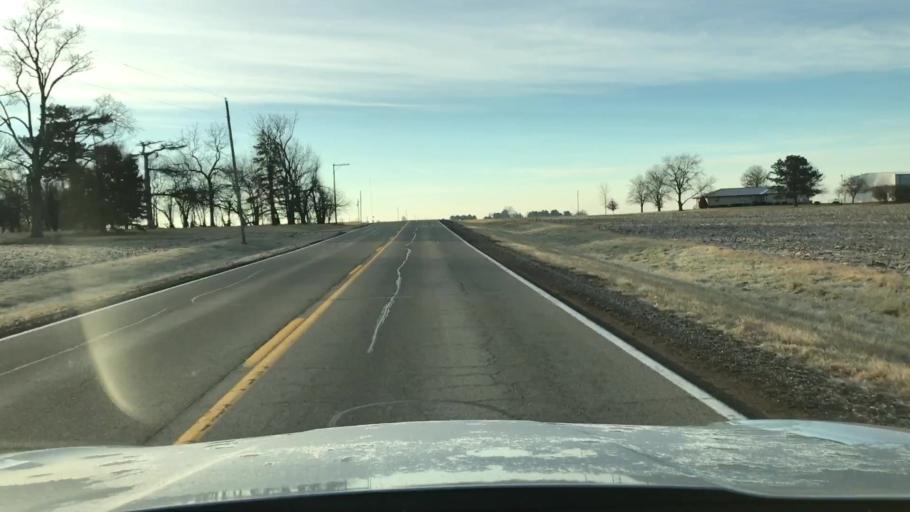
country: US
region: Illinois
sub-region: McLean County
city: Hudson
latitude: 40.5934
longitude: -88.9448
